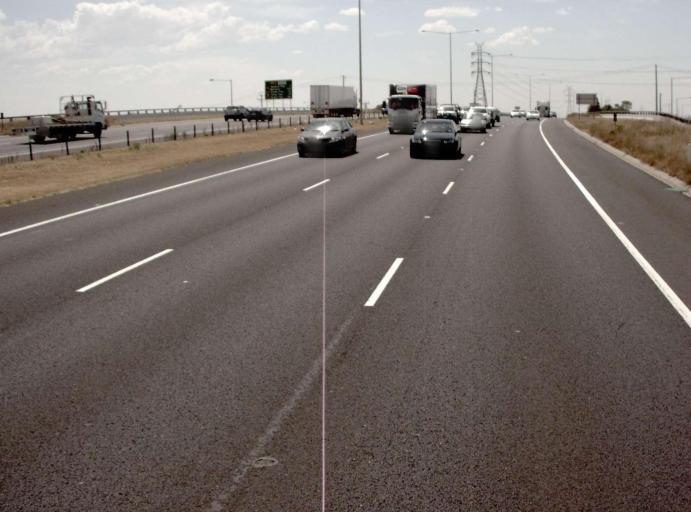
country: AU
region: Victoria
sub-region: Brimbank
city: Sunshine West
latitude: -37.8178
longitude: 144.8090
